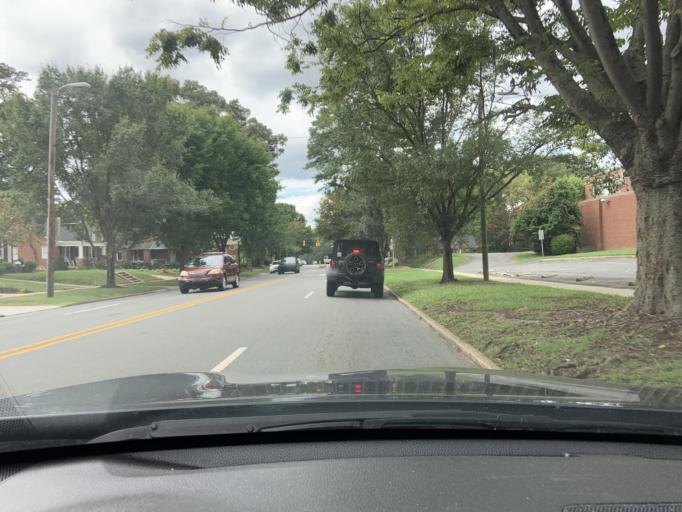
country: US
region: North Carolina
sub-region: Mecklenburg County
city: Charlotte
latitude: 35.2153
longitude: -80.8645
